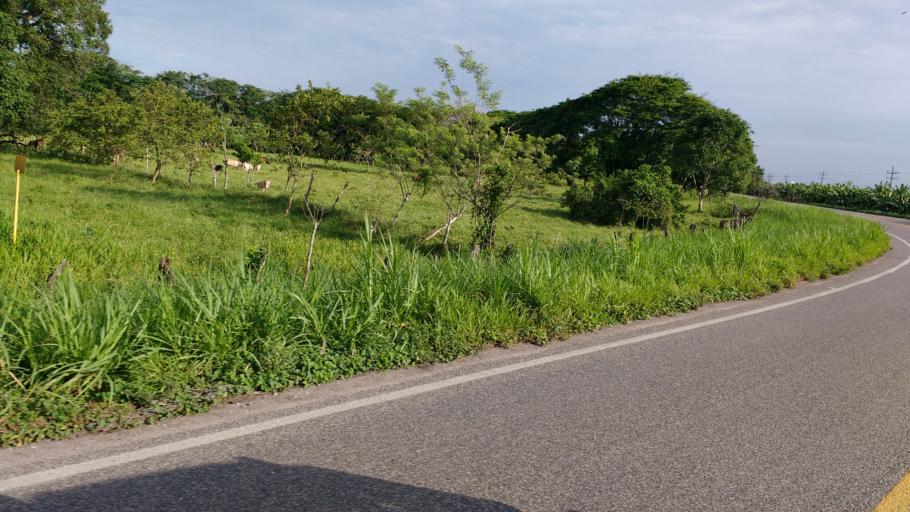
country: MX
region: Tabasco
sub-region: Teapa
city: Eureka y Belen
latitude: 17.6238
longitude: -92.9622
